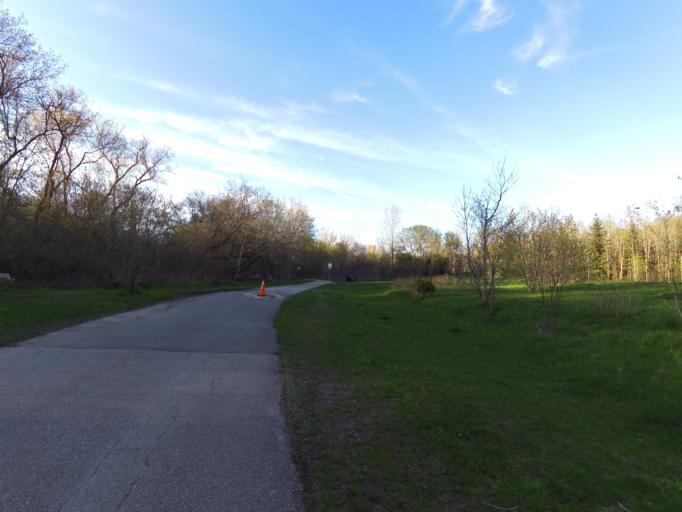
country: CA
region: Ontario
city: Toronto
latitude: 43.6958
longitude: -79.3560
